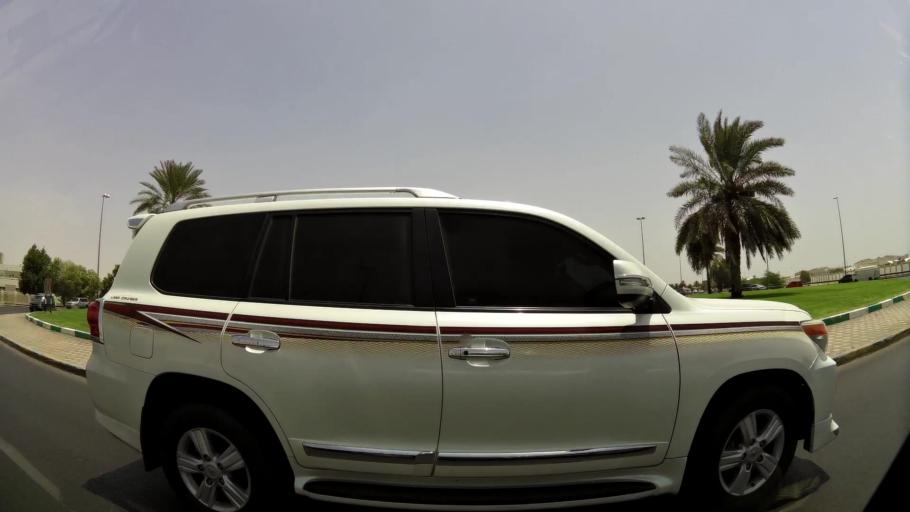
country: AE
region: Abu Dhabi
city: Al Ain
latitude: 24.2045
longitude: 55.7467
